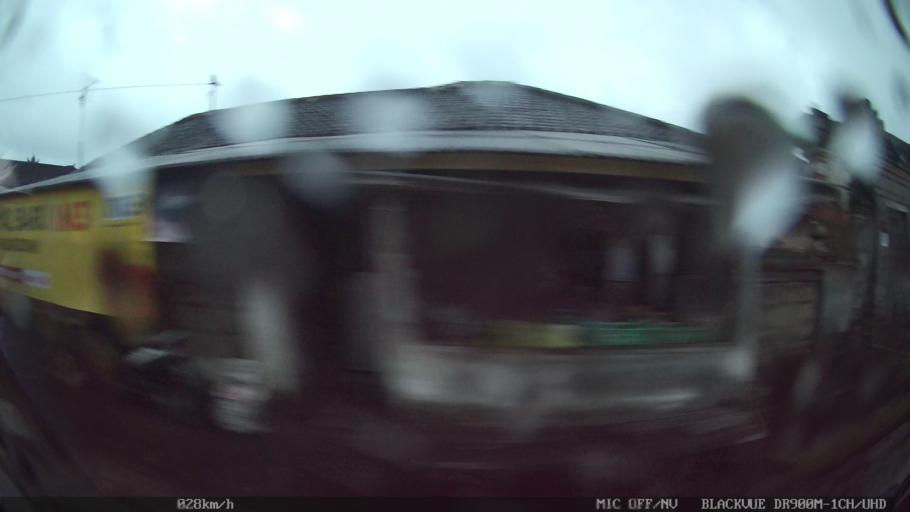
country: ID
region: Bali
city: Banjar Sedang
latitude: -8.5620
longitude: 115.2516
